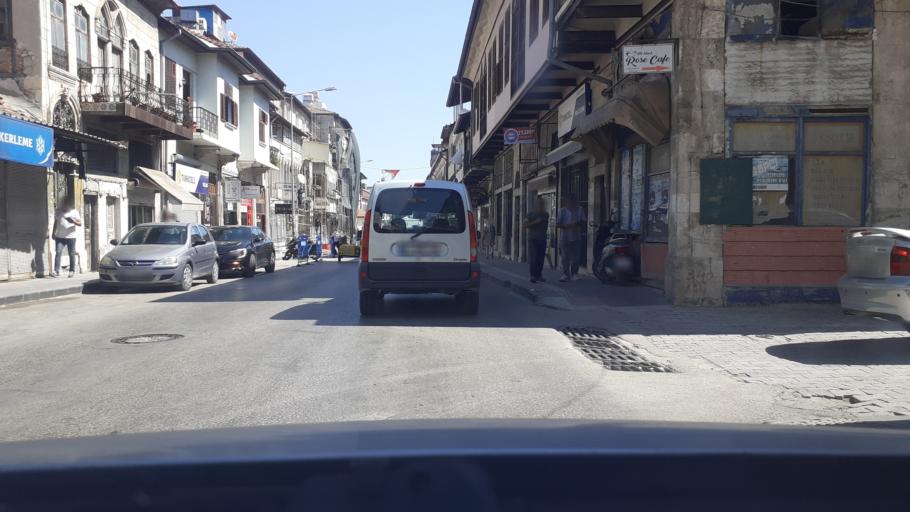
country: TR
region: Hatay
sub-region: Antakya Ilcesi
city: Antakya
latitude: 36.1987
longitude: 36.1629
